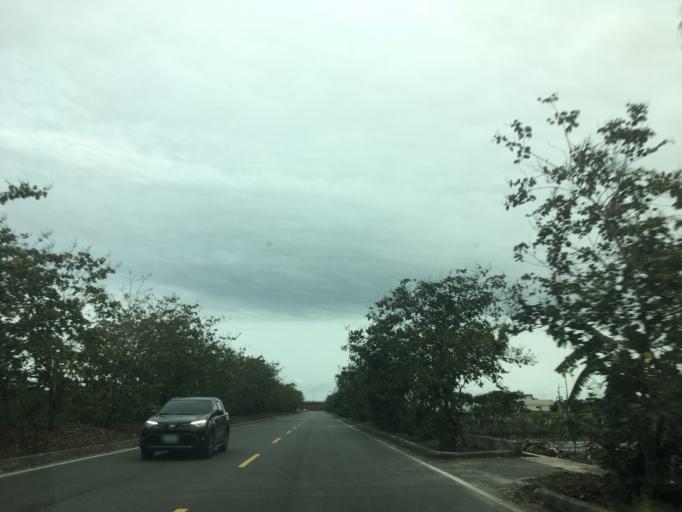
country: TW
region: Taiwan
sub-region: Taitung
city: Taitung
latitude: 22.7945
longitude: 121.1379
